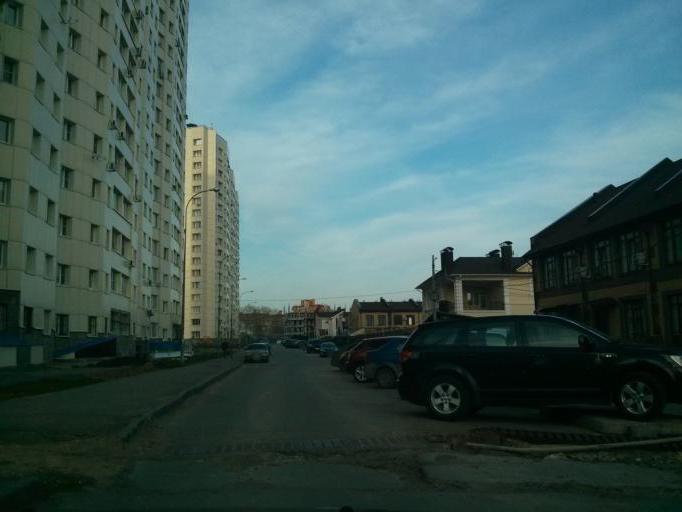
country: RU
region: Nizjnij Novgorod
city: Afonino
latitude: 56.2837
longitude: 44.0721
